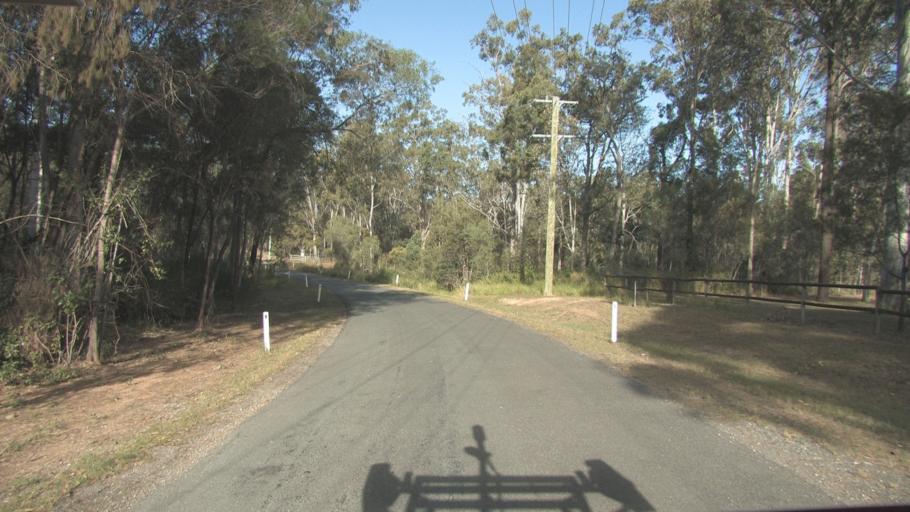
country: AU
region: Queensland
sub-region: Logan
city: Cedar Vale
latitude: -27.8268
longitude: 153.0667
